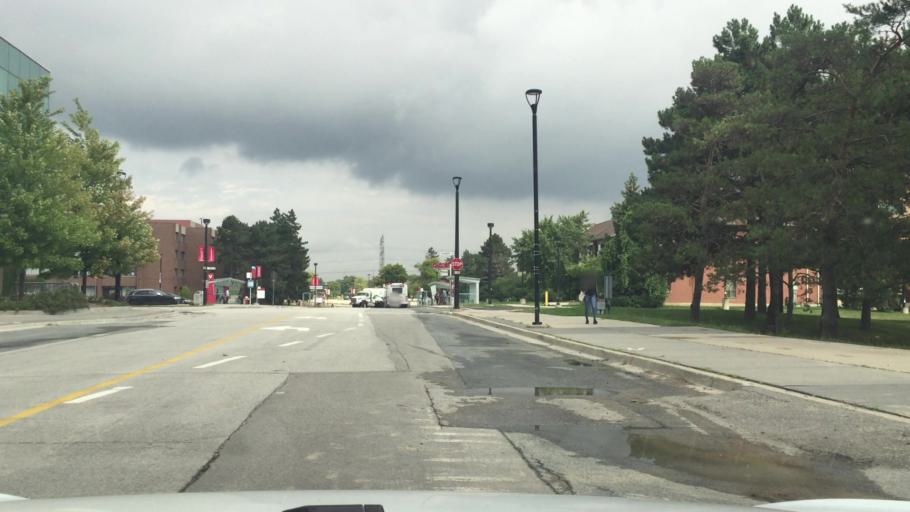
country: CA
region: Ontario
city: Concord
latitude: 43.7749
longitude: -79.5000
